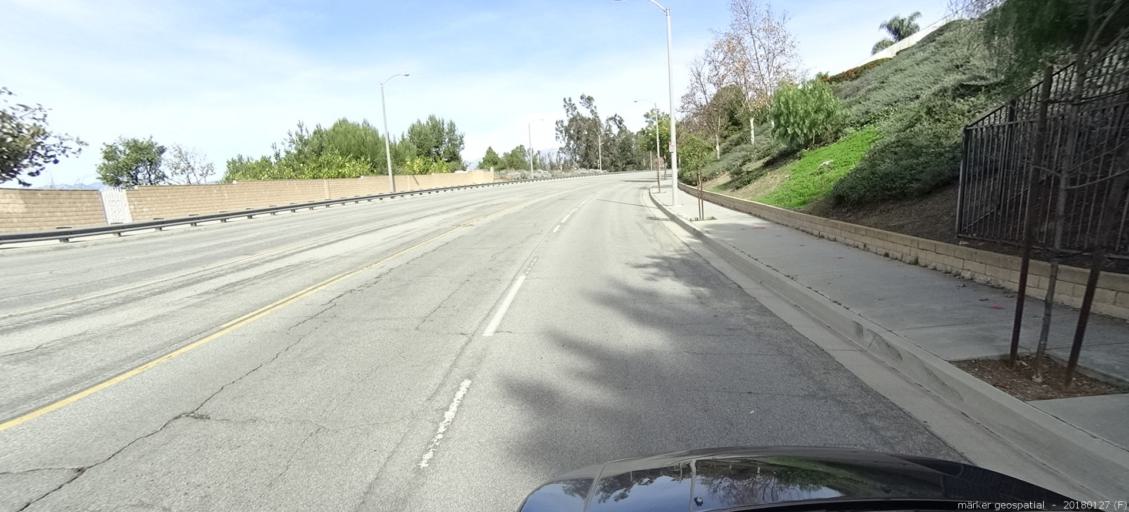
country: US
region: California
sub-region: Los Angeles County
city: Walnut
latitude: 33.9806
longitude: -117.8551
